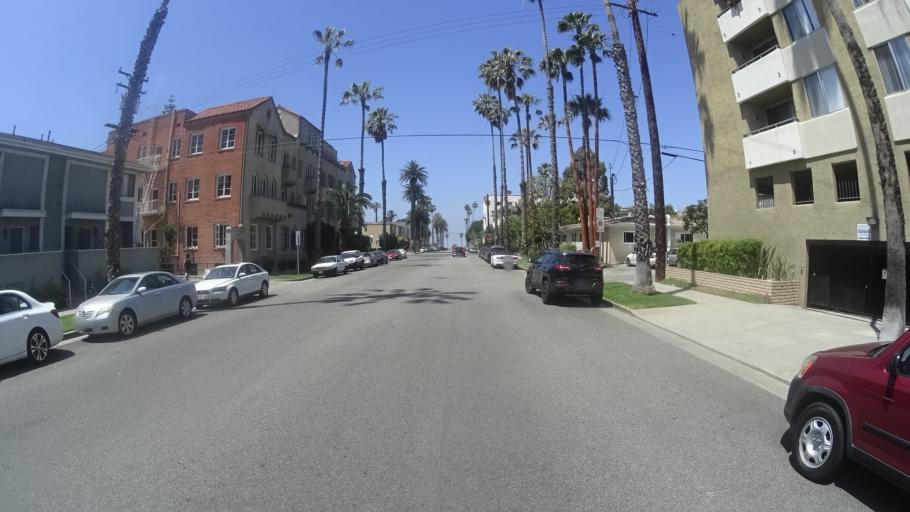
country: US
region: California
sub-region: Los Angeles County
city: Santa Monica
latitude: 34.0216
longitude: -118.5016
